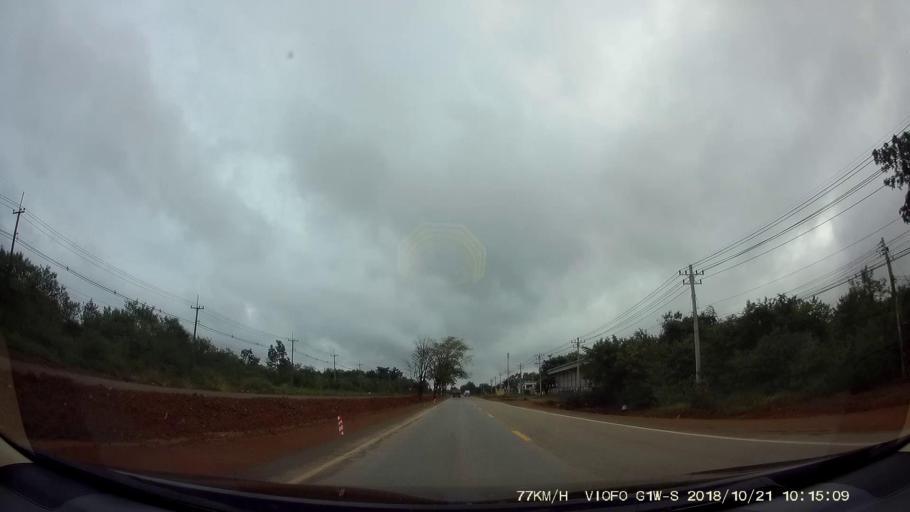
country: TH
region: Chaiyaphum
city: Phu Khiao
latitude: 16.3433
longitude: 102.1628
